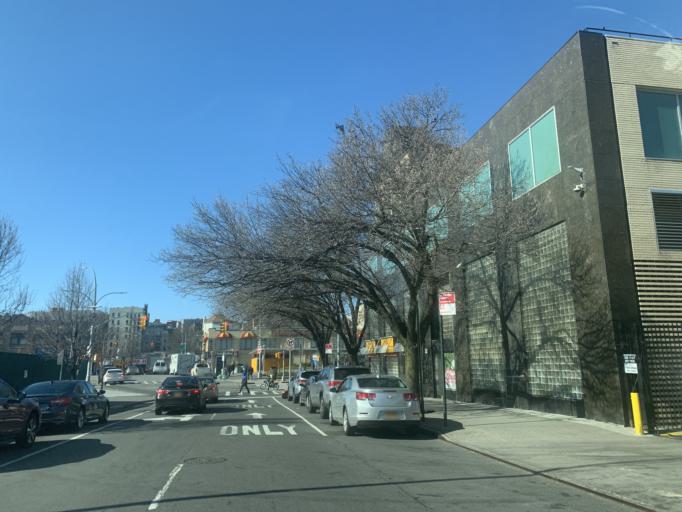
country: US
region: New York
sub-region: Bronx
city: The Bronx
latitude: 40.8599
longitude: -73.8910
